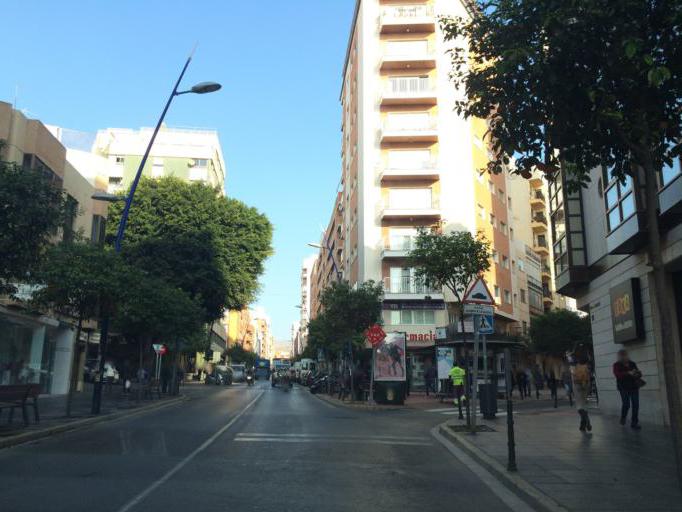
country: ES
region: Andalusia
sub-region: Provincia de Almeria
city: Almeria
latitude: 36.8425
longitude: -2.4641
